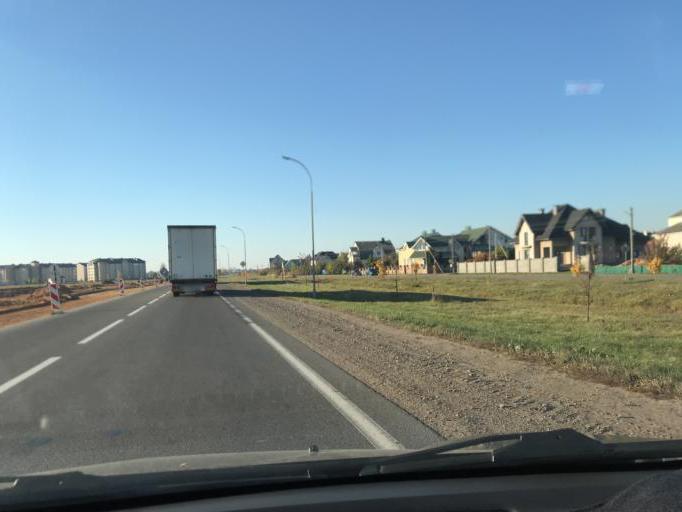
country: BY
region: Minsk
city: Slutsk
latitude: 53.0444
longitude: 27.5751
